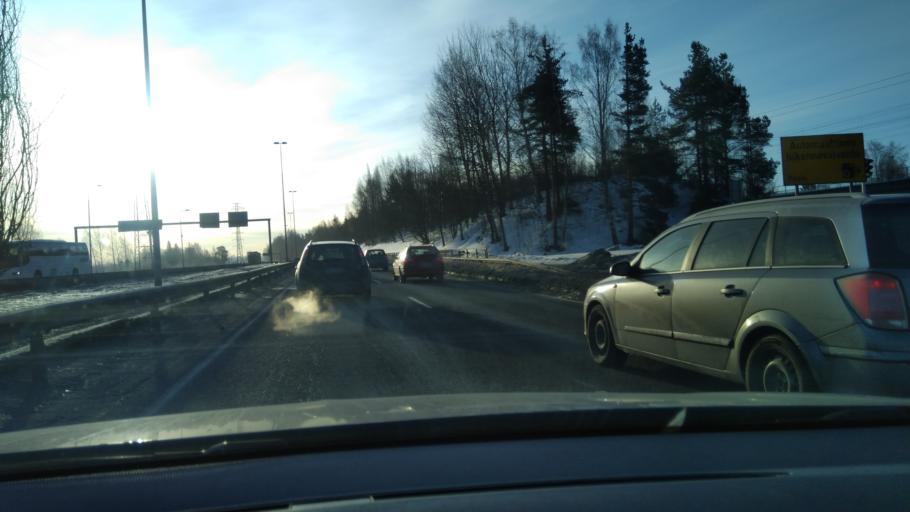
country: FI
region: Pirkanmaa
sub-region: Tampere
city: Pirkkala
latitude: 61.5096
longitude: 23.6906
